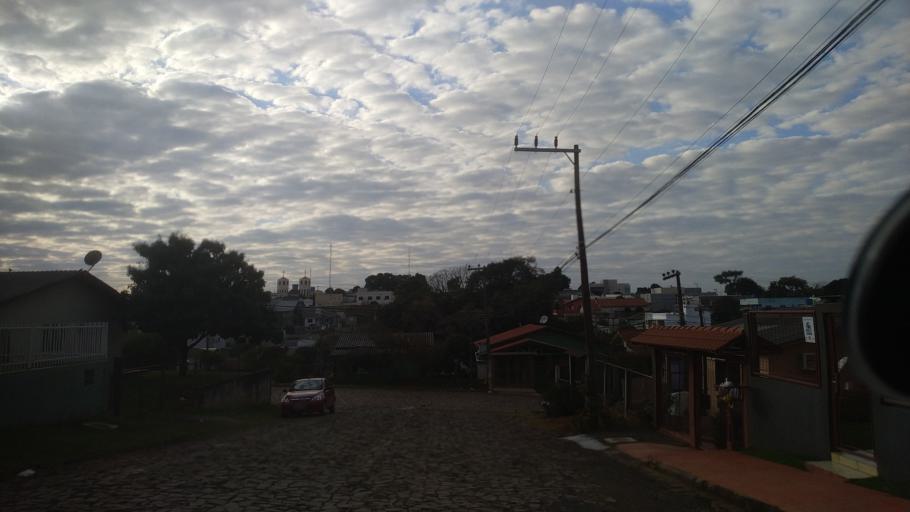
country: BR
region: Santa Catarina
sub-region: Chapeco
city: Chapeco
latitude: -27.0988
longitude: -52.6767
